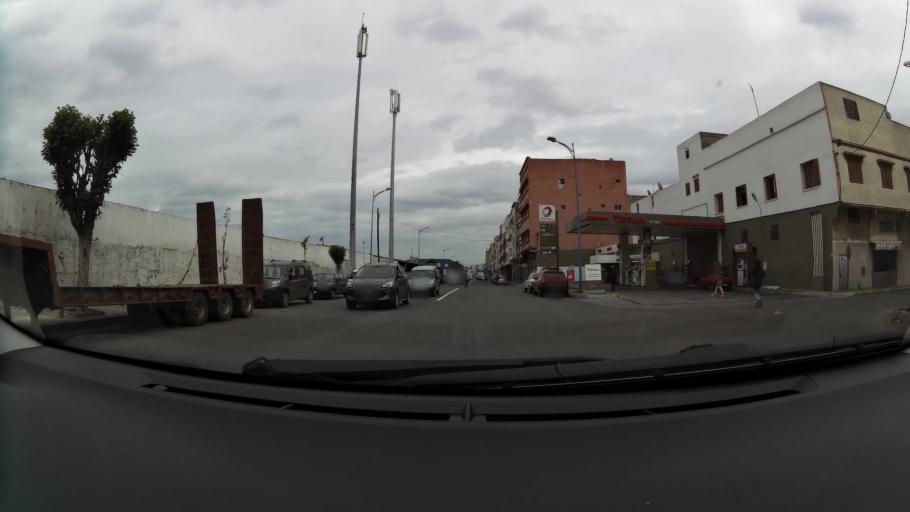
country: MA
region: Grand Casablanca
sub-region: Casablanca
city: Casablanca
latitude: 33.5957
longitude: -7.5641
